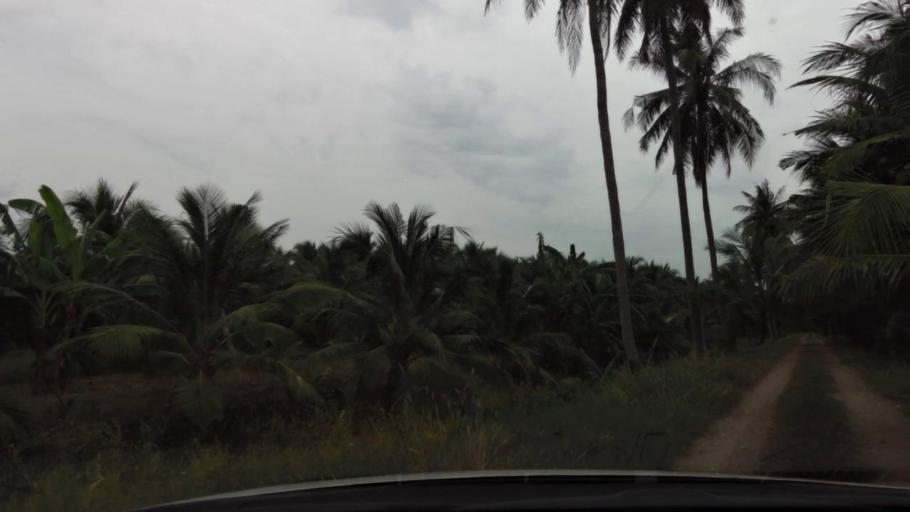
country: TH
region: Samut Sakhon
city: Ban Phaeo
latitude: 13.6122
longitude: 100.0270
